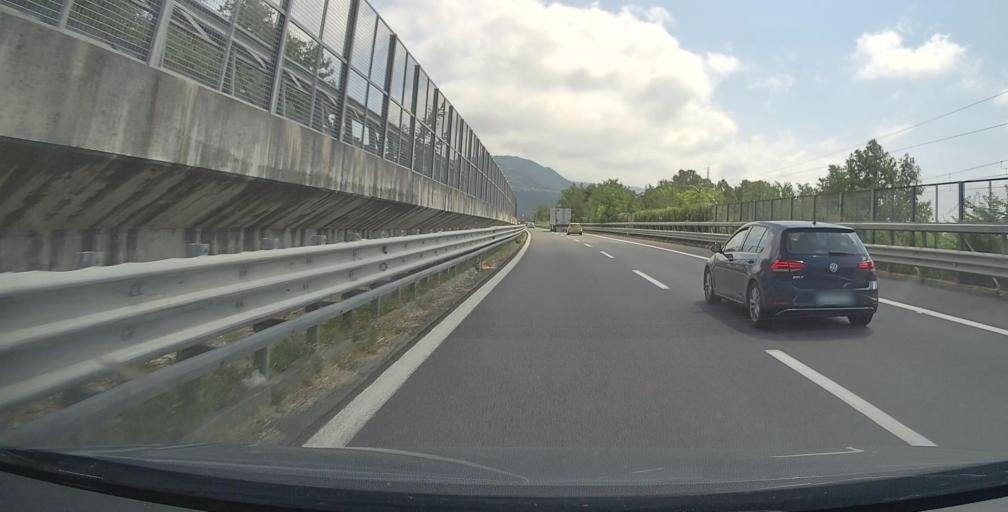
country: IT
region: Calabria
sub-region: Provincia di Vibo-Valentia
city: Pizzo
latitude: 38.7850
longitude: 16.2190
